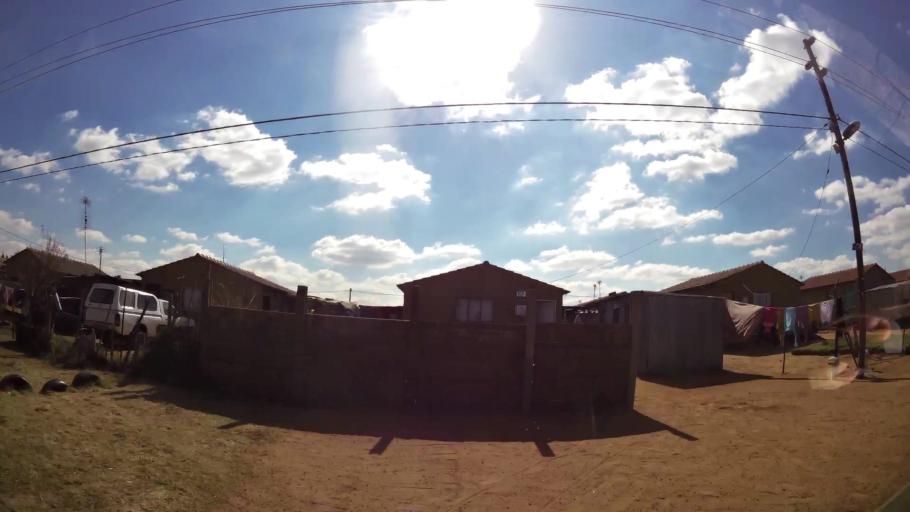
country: ZA
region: Gauteng
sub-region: West Rand District Municipality
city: Krugersdorp
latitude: -26.1468
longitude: 27.7829
